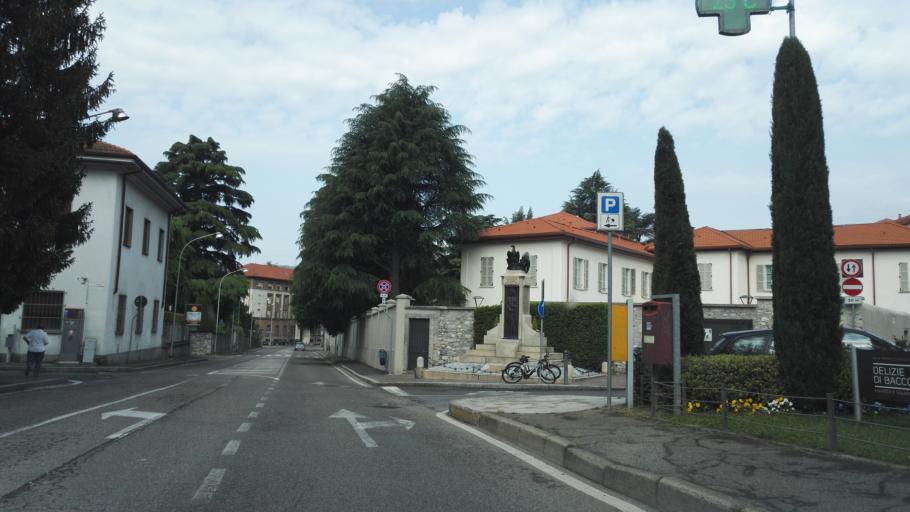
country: IT
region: Lombardy
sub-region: Provincia di Como
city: Brunate
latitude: 45.8058
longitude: 9.0978
